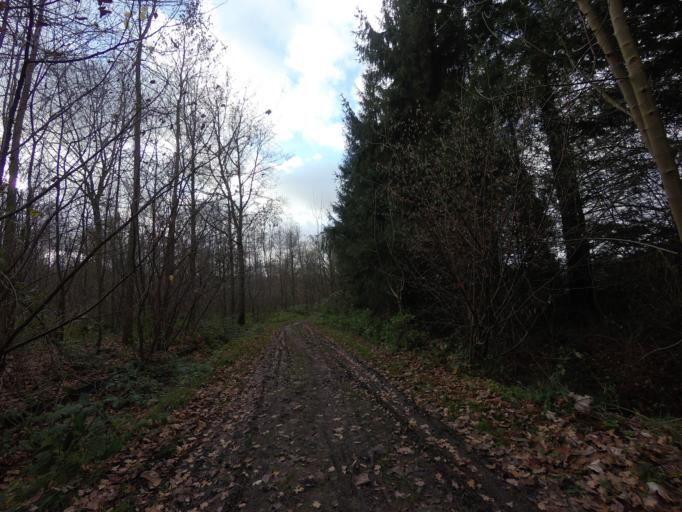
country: BE
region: Flanders
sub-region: Provincie Vlaams-Brabant
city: Haacht
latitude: 50.9581
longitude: 4.6237
